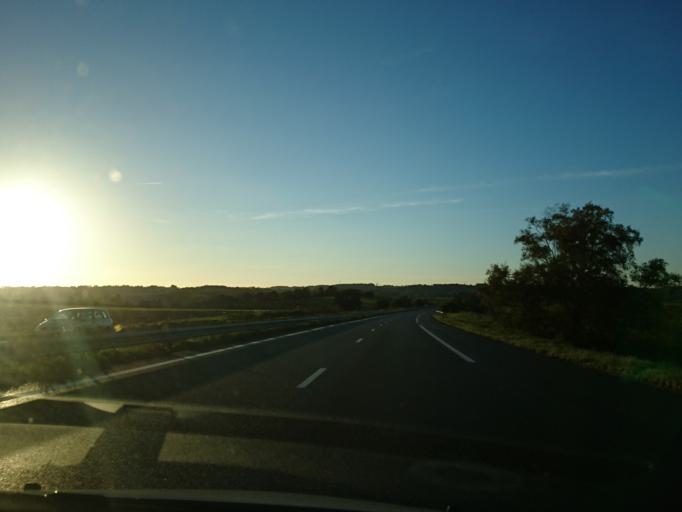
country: FR
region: Brittany
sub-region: Departement du Finistere
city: Guerlesquin
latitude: 48.5712
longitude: -3.6229
